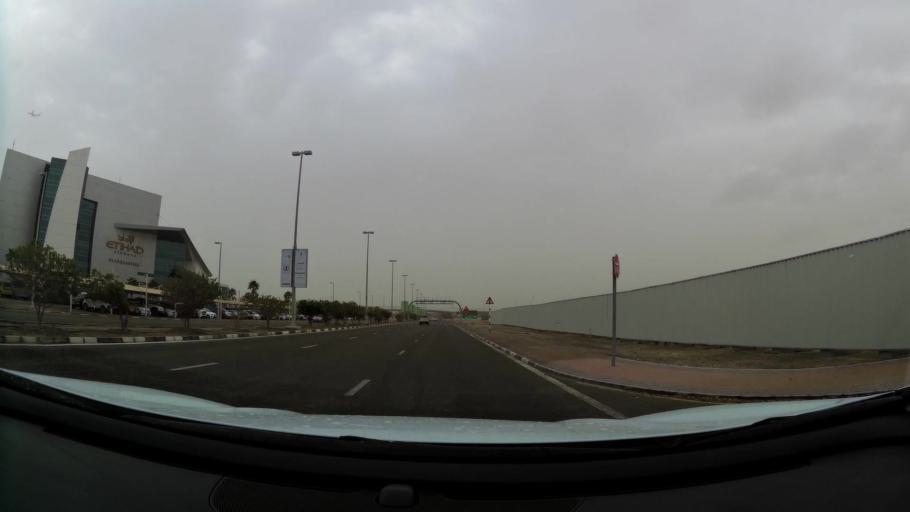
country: AE
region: Abu Dhabi
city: Abu Dhabi
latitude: 24.4451
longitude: 54.6135
